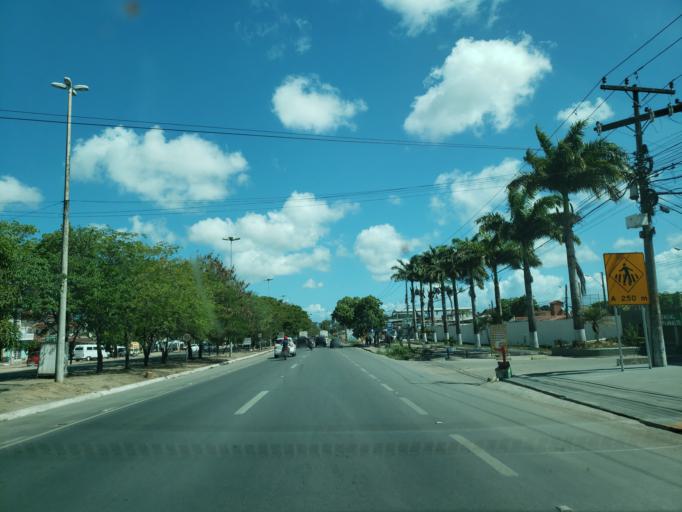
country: BR
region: Alagoas
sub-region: Satuba
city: Satuba
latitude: -9.5429
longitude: -35.7900
